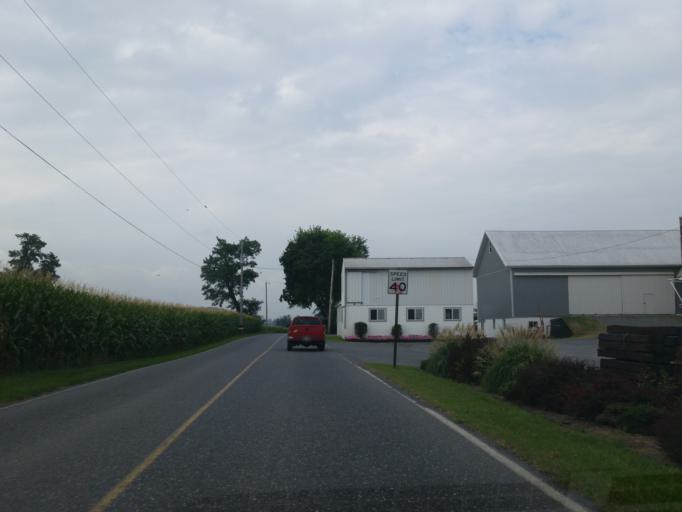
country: US
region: Pennsylvania
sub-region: Lebanon County
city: Richland
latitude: 40.3357
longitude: -76.2640
